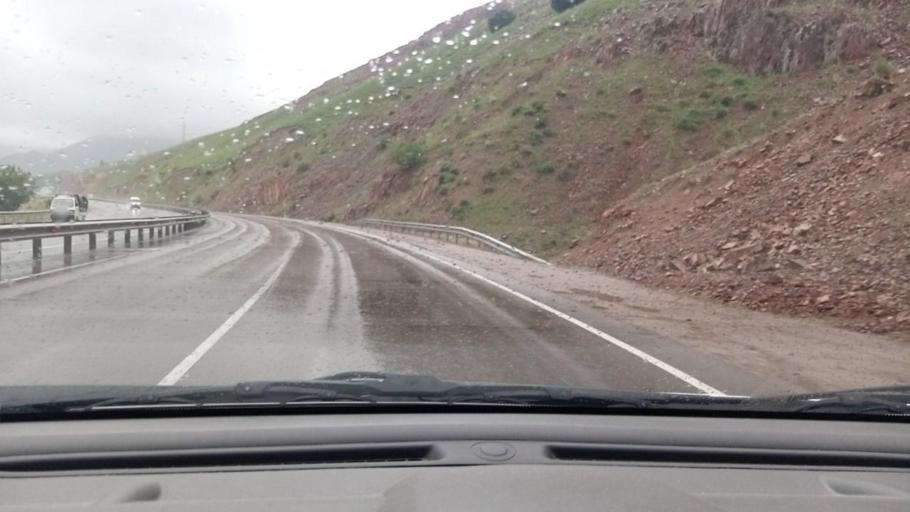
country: UZ
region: Toshkent
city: Angren
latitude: 41.1158
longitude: 70.3413
